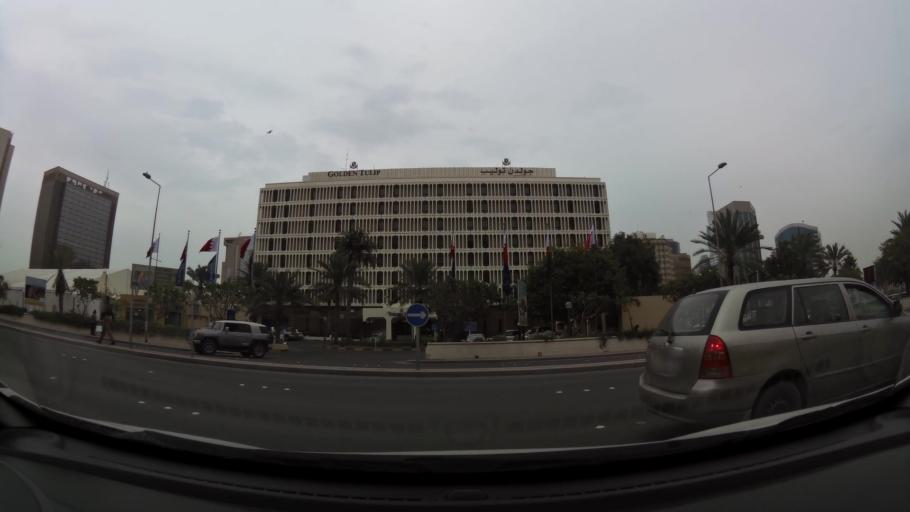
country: BH
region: Manama
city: Manama
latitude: 26.2397
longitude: 50.5841
